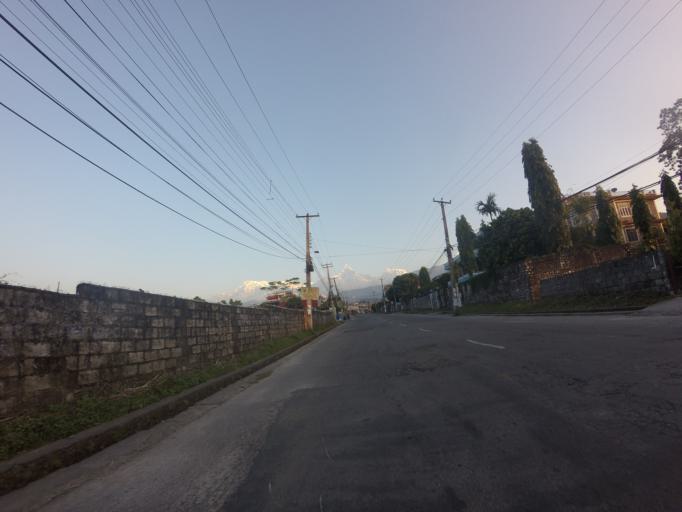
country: NP
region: Western Region
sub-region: Gandaki Zone
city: Pokhara
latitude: 28.2167
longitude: 83.9978
